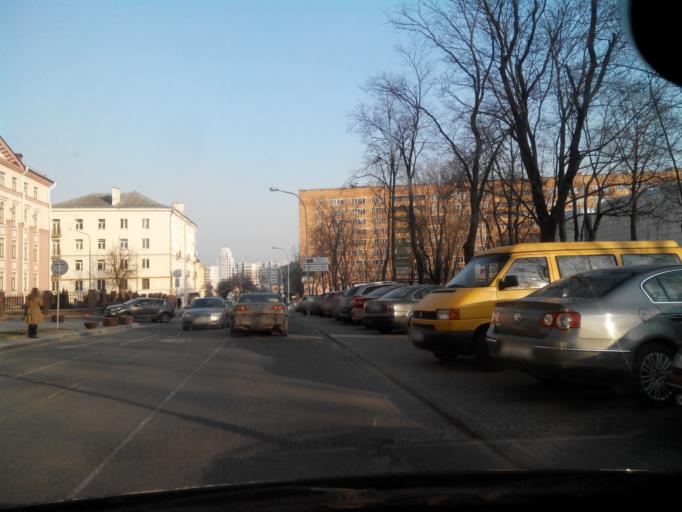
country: BY
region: Minsk
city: Minsk
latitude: 53.9058
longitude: 27.5421
